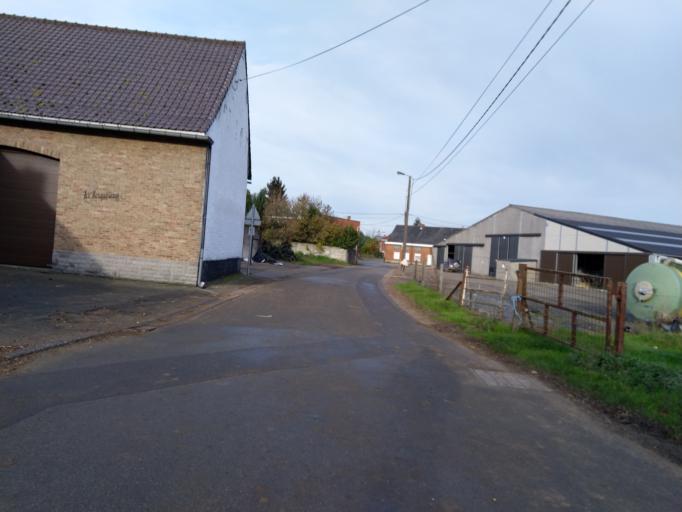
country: BE
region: Wallonia
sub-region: Province du Hainaut
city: Jurbise
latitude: 50.5141
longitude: 3.8521
